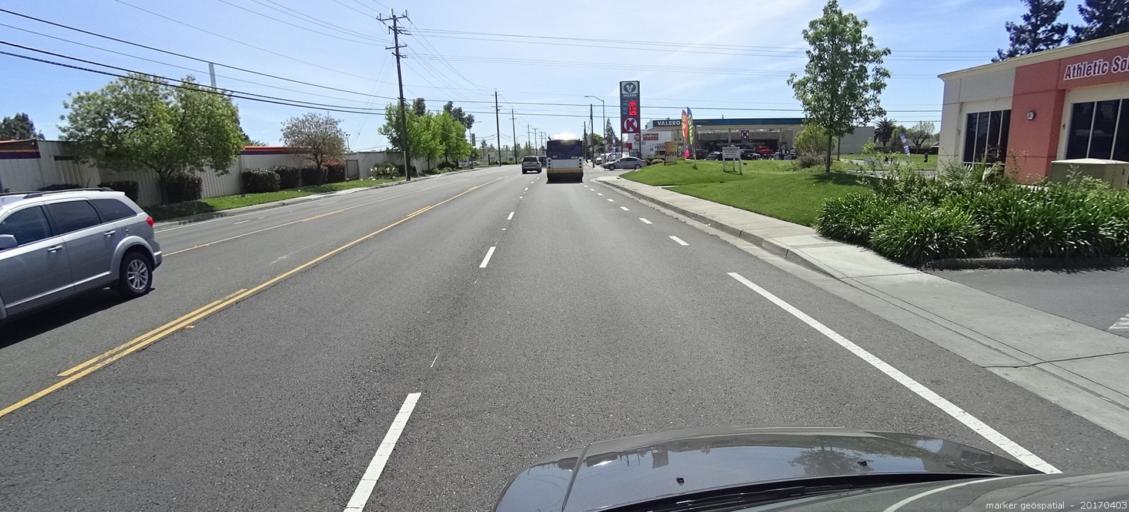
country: US
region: California
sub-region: Sacramento County
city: Sacramento
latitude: 38.6281
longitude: -121.4756
